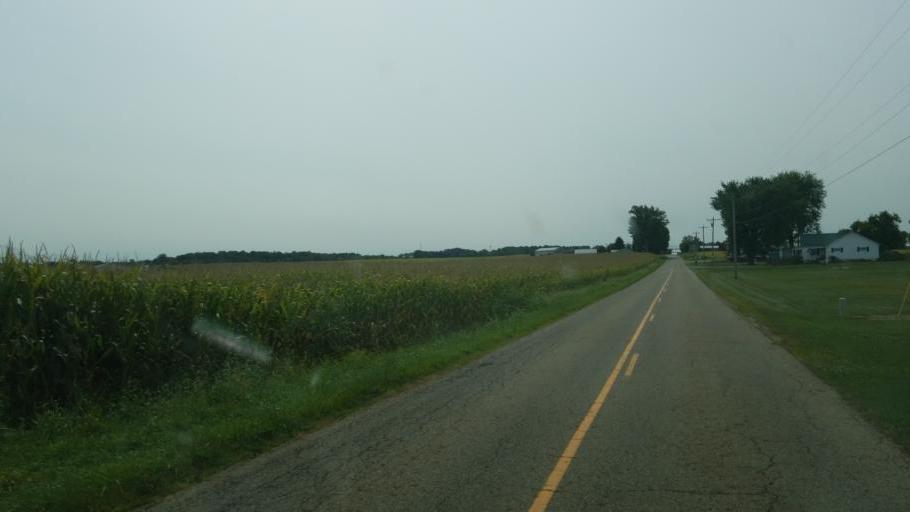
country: US
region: Ohio
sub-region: Knox County
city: Fredericktown
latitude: 40.4530
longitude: -82.5729
